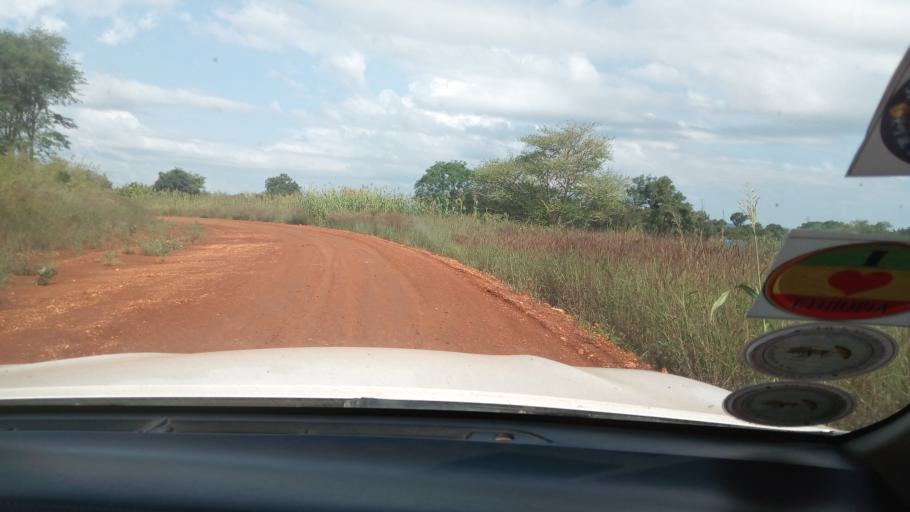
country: ET
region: Oromiya
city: Mendi
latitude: 10.1680
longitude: 35.0263
